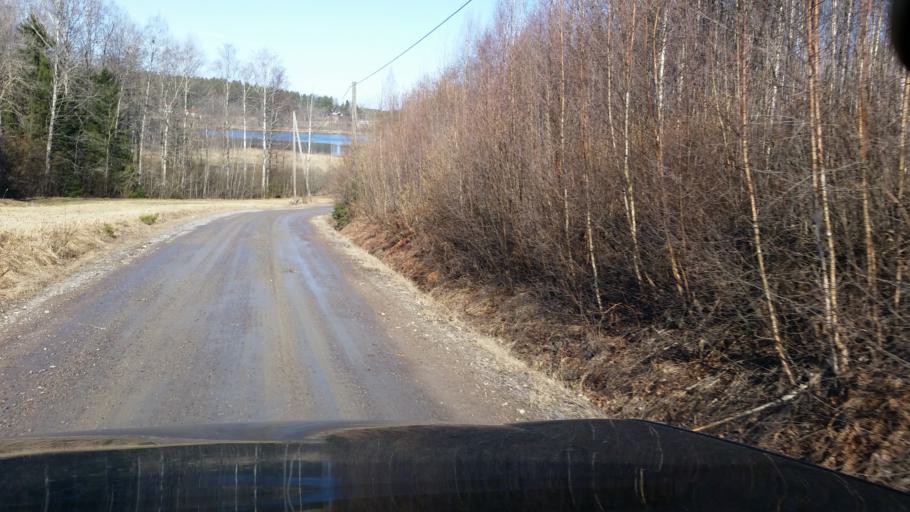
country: FI
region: Uusimaa
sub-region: Helsinki
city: Karjalohja
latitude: 60.2147
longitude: 23.6953
